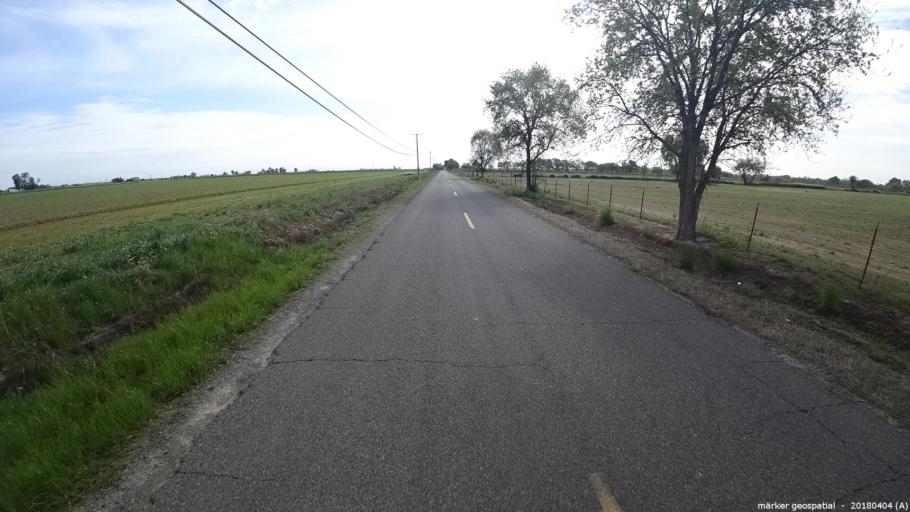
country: US
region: California
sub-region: Sacramento County
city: Herald
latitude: 38.2556
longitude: -121.2322
